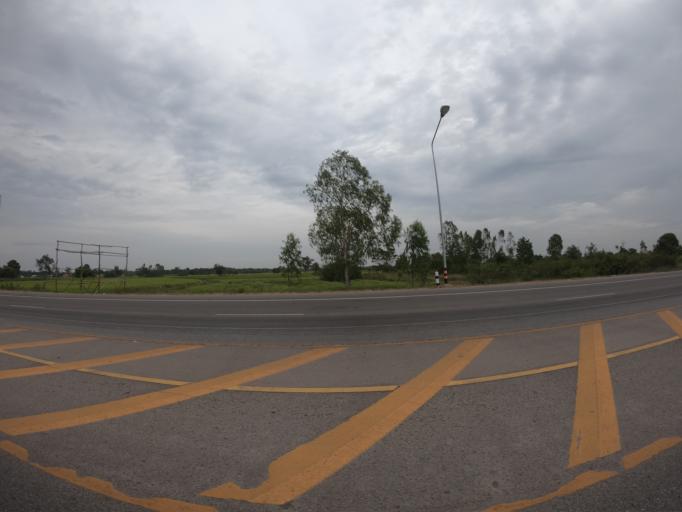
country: TH
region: Roi Et
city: Chiang Khwan
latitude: 16.1385
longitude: 103.8562
